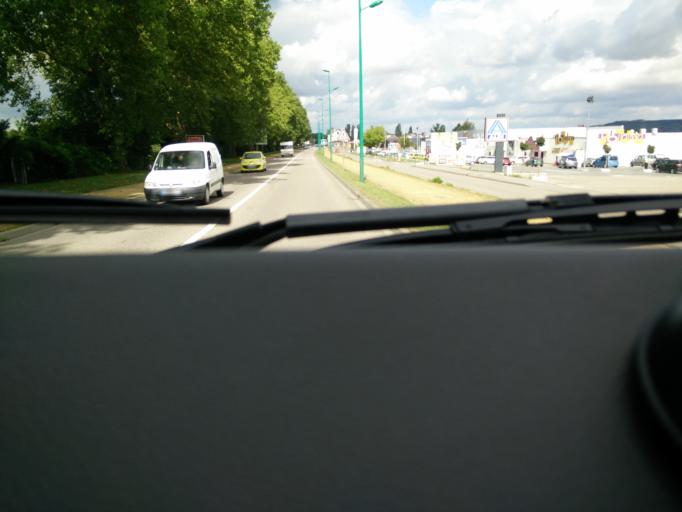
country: FR
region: Lorraine
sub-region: Departement de la Meuse
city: Verdun
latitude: 49.1460
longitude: 5.4064
